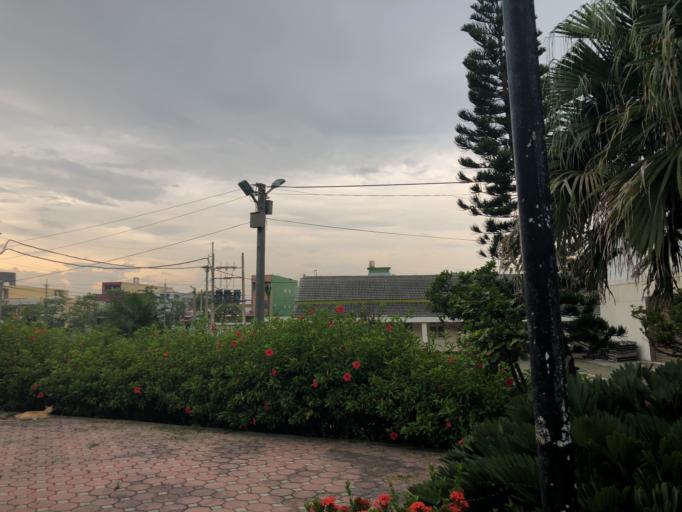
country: TW
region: Taiwan
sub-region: Chiayi
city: Taibao
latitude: 23.7179
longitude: 120.2015
